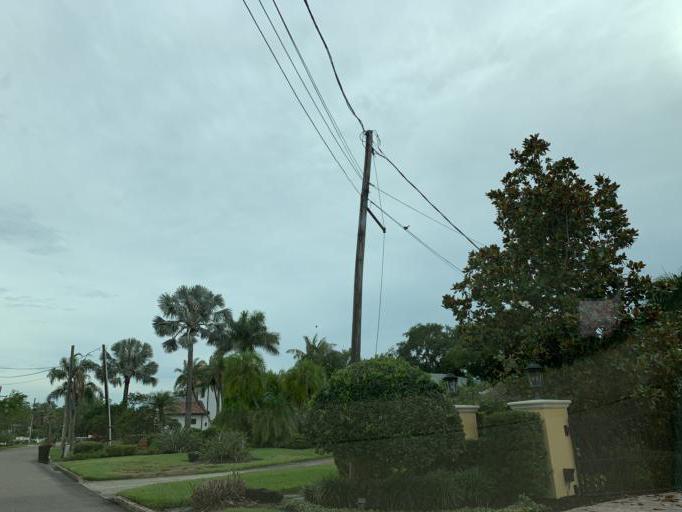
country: US
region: Florida
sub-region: Pinellas County
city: Gandy
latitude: 27.7951
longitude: -82.6065
